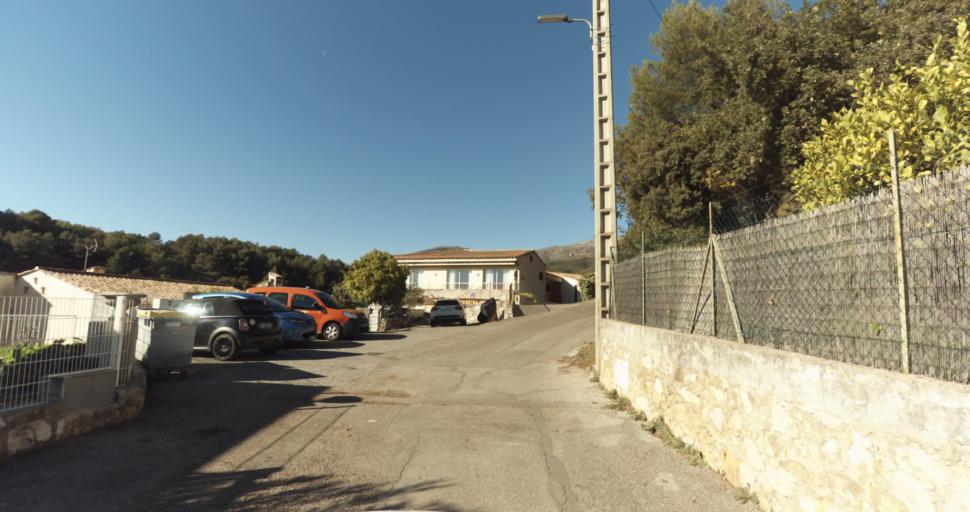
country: FR
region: Provence-Alpes-Cote d'Azur
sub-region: Departement des Alpes-Maritimes
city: Vence
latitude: 43.7198
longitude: 7.1011
